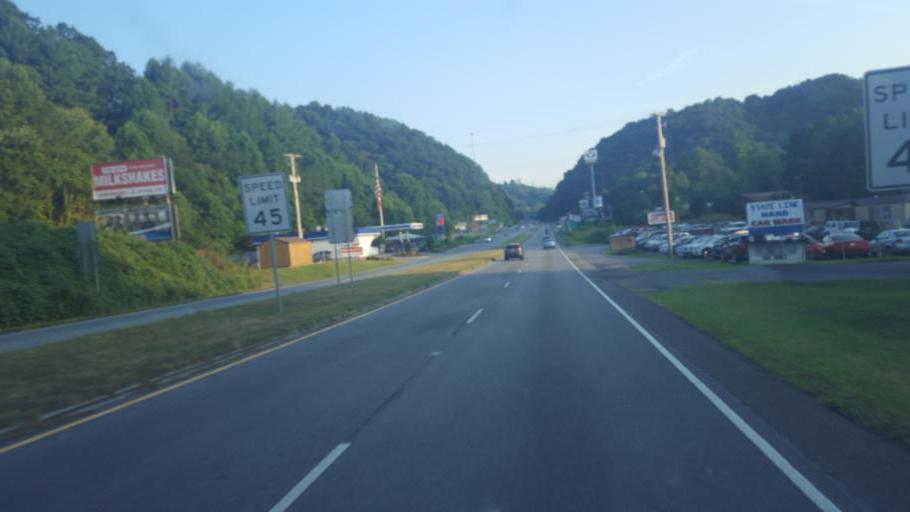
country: US
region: Virginia
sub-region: Scott County
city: Weber City
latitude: 36.6019
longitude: -82.5706
